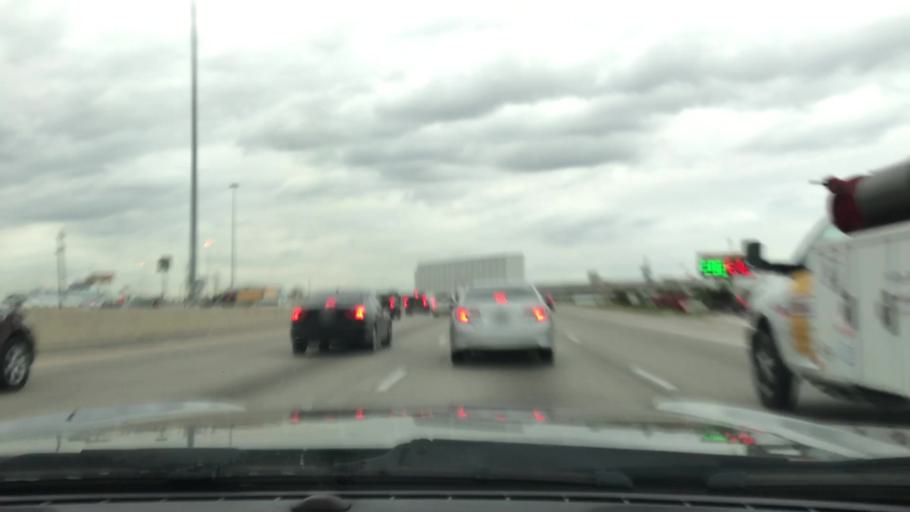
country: US
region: Texas
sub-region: Harris County
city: Jacinto City
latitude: 29.7936
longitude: -95.2686
